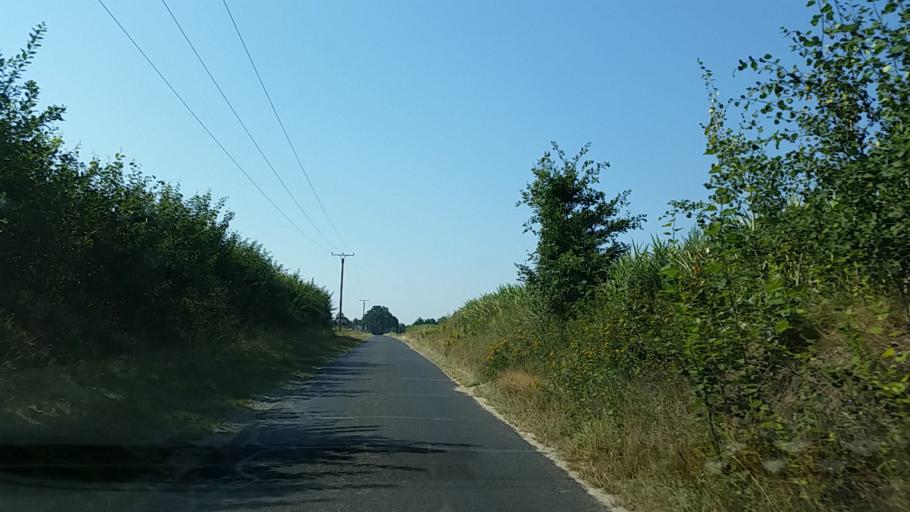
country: DE
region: Lower Saxony
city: Hankensbuttel
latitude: 52.7196
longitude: 10.6289
